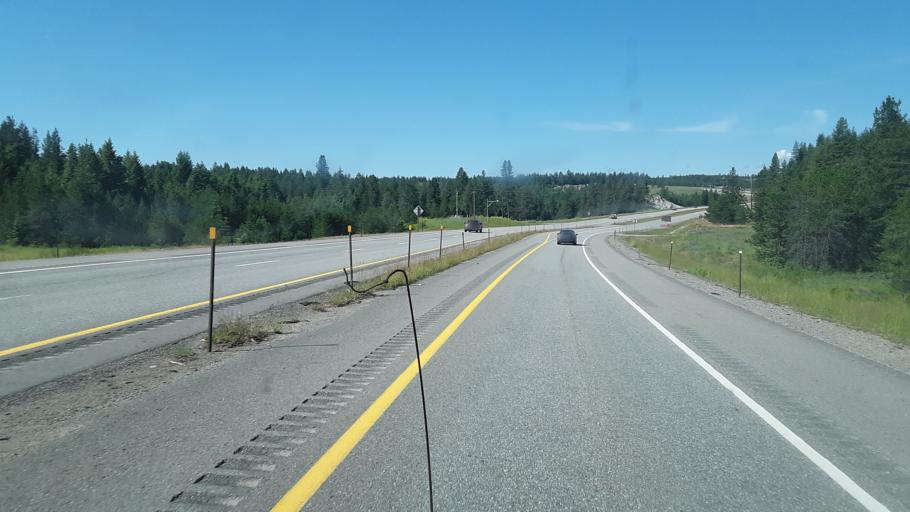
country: US
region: Idaho
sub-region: Kootenai County
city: Spirit Lake
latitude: 47.9937
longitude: -116.6797
